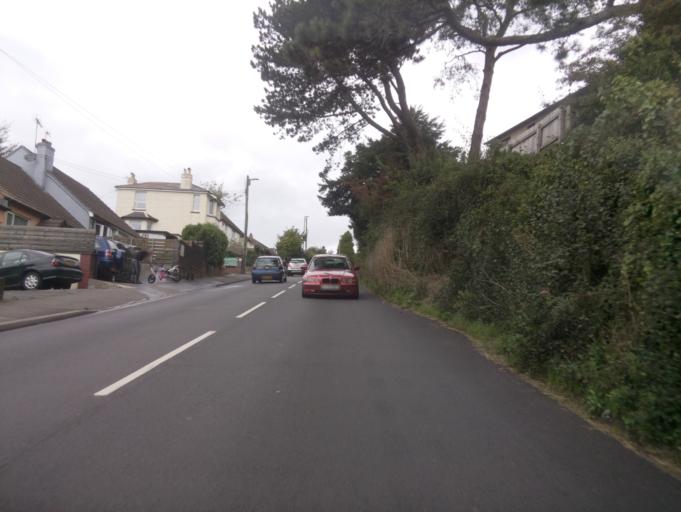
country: GB
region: England
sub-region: Devon
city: Marldon
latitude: 50.4369
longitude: -3.5890
